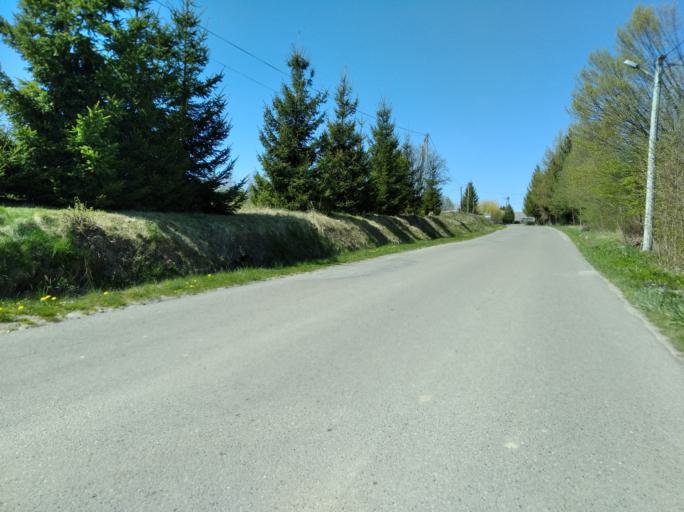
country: PL
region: Subcarpathian Voivodeship
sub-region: Powiat brzozowski
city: Jablonka
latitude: 49.7244
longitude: 22.1146
